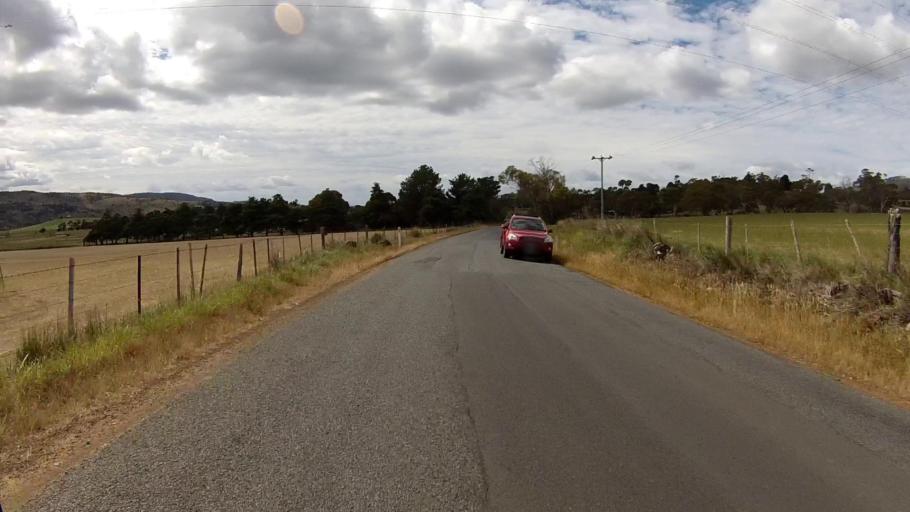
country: AU
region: Tasmania
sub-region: Clarence
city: Cambridge
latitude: -42.7696
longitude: 147.4090
